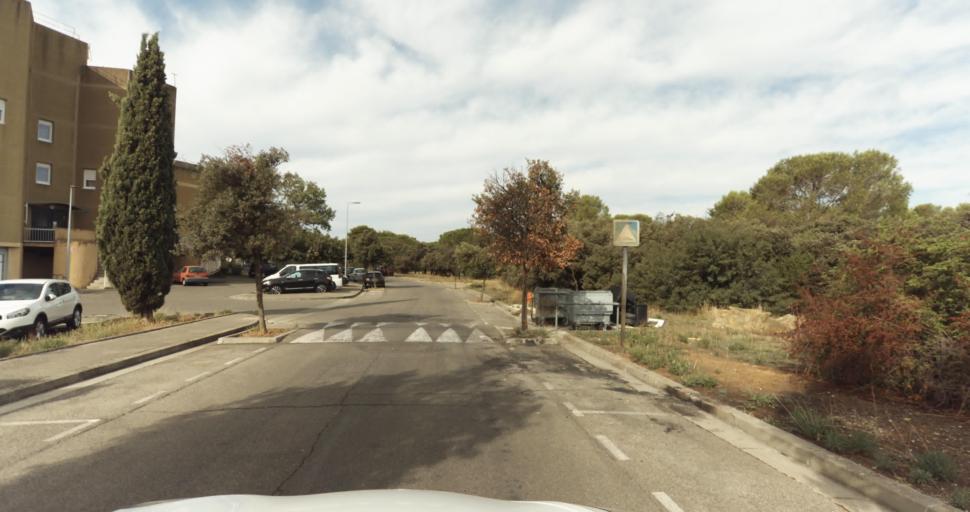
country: FR
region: Provence-Alpes-Cote d'Azur
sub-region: Departement des Bouches-du-Rhone
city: Miramas
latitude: 43.6006
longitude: 5.0090
